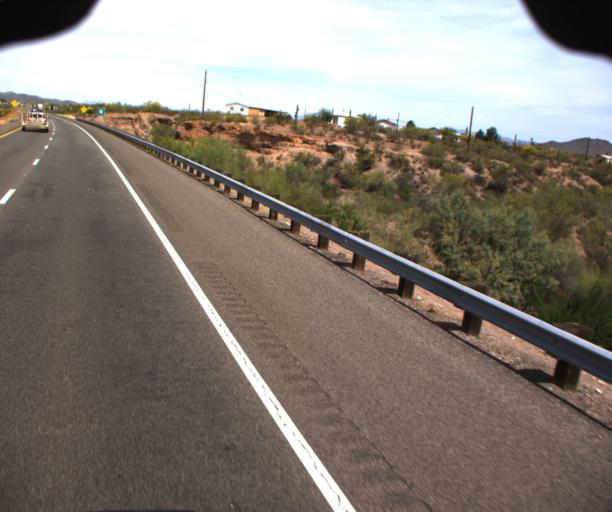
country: US
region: Arizona
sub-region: Maricopa County
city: Wickenburg
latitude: 33.8582
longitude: -112.6265
